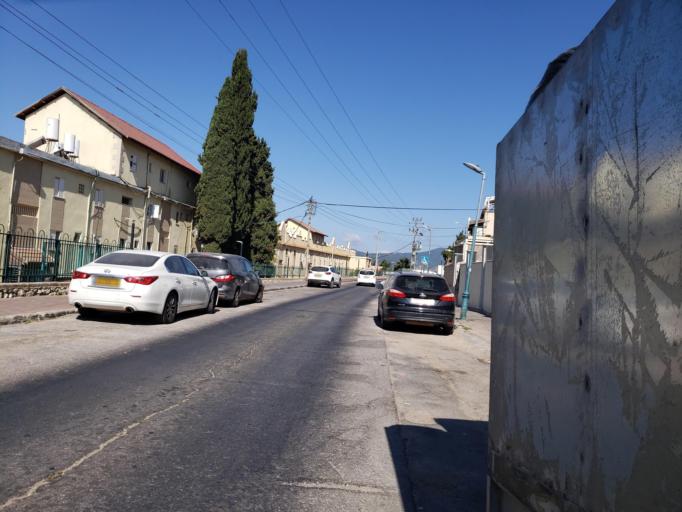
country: IL
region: Northern District
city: Safed
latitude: 32.9562
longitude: 35.4967
